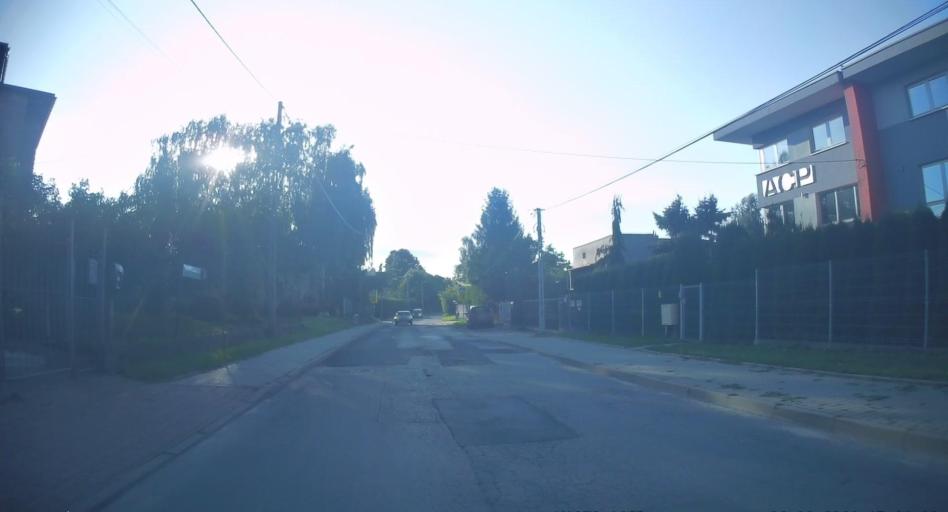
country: PL
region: Lesser Poland Voivodeship
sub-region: Powiat wielicki
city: Czarnochowice
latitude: 50.0175
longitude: 20.0449
